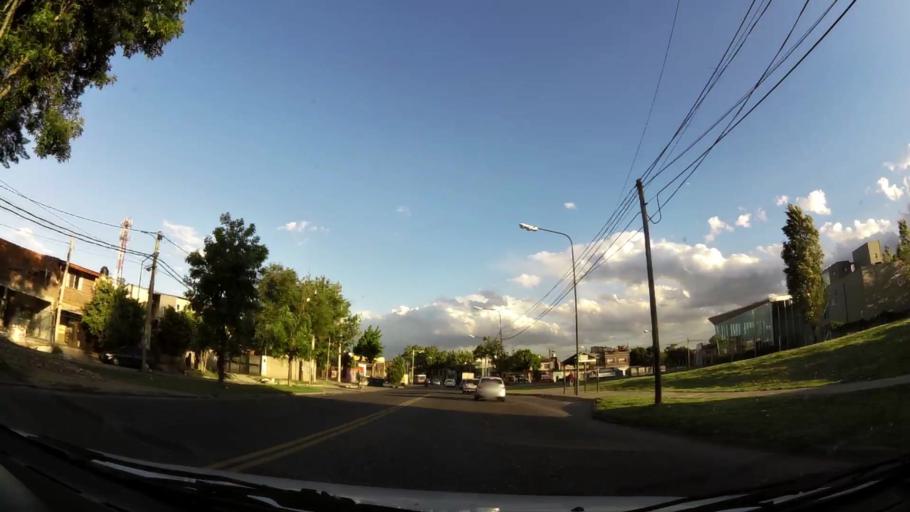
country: AR
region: Buenos Aires
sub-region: Partido de San Isidro
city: San Isidro
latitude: -34.4718
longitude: -58.5383
